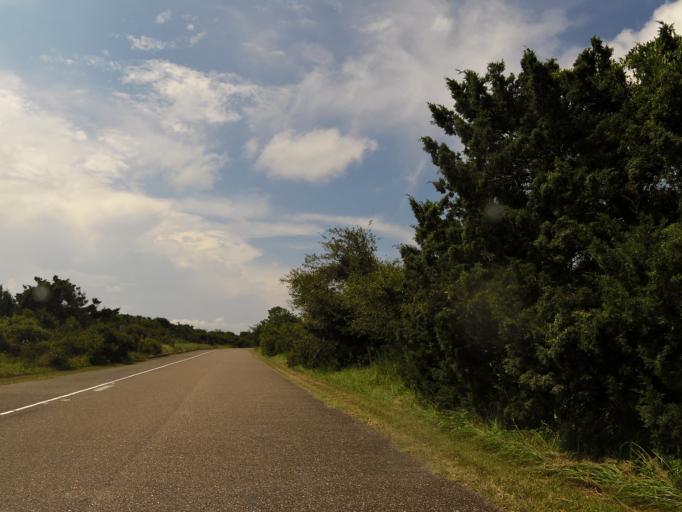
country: US
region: Florida
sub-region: Duval County
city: Atlantic Beach
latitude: 30.4489
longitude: -81.4143
